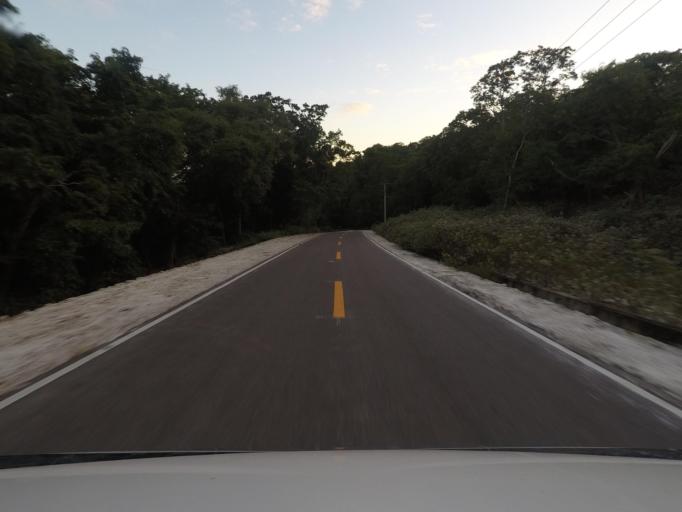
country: TL
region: Lautem
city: Lospalos
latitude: -8.4096
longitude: 127.2900
